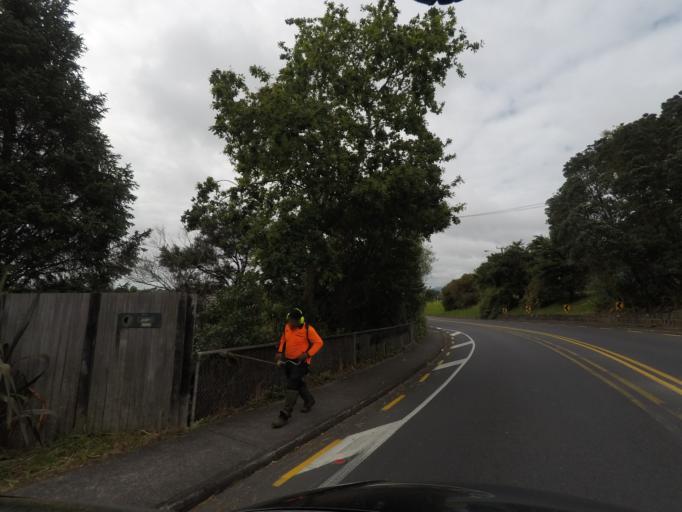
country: NZ
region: Auckland
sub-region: Auckland
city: Rosebank
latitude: -36.8381
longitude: 174.6005
